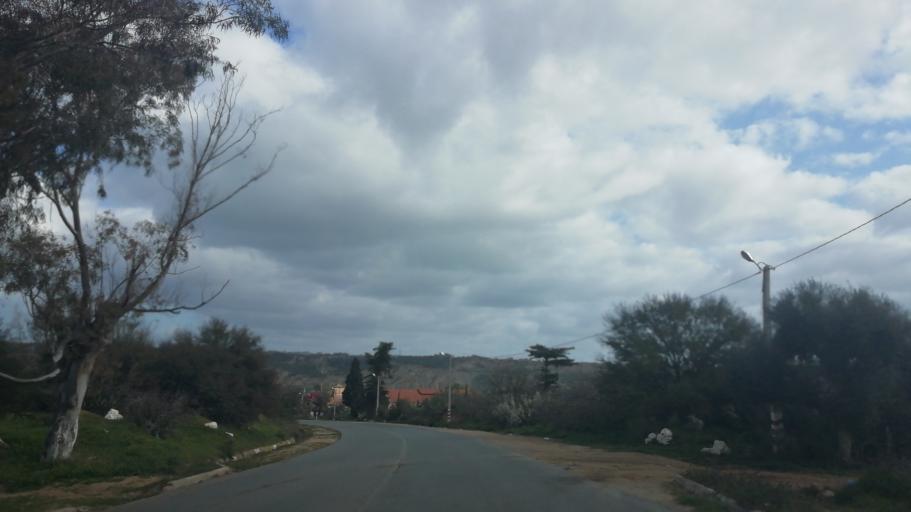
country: DZ
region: Relizane
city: Mazouna
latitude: 36.2961
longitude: 0.6575
